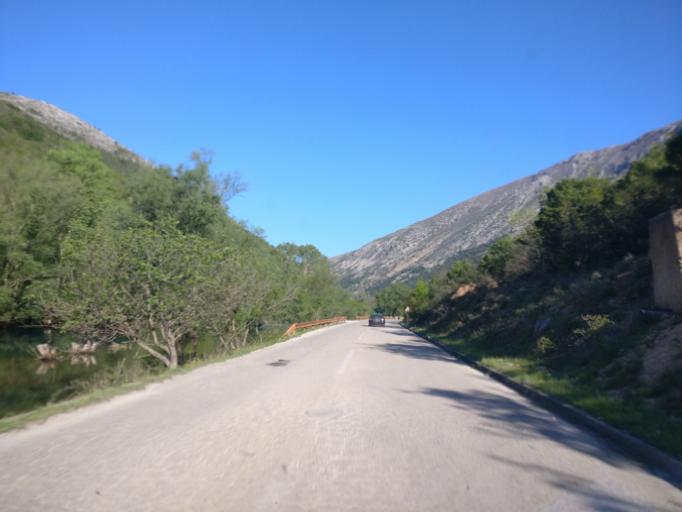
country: BA
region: Federation of Bosnia and Herzegovina
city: Stolac
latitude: 43.0889
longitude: 17.9998
